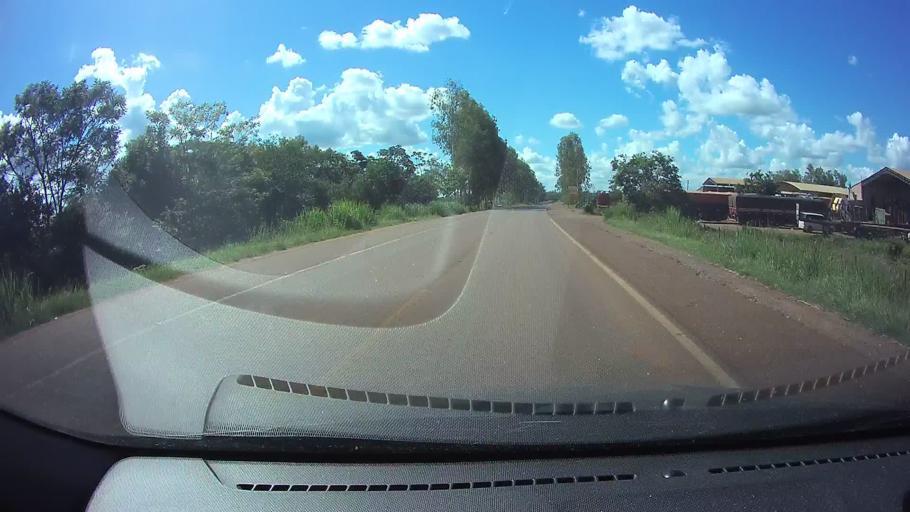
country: PY
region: Guaira
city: Coronel Martinez
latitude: -25.7866
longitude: -56.6477
